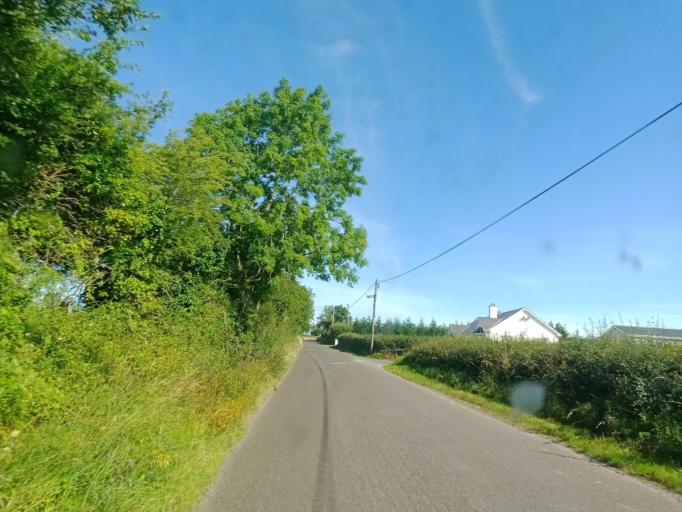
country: IE
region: Leinster
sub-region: Kilkenny
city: Ballyragget
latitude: 52.7631
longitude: -7.4078
